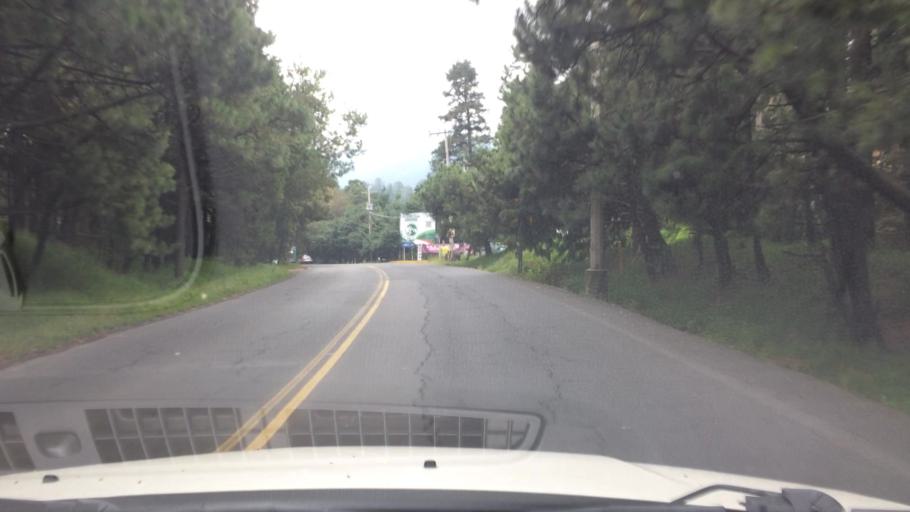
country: MX
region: Mexico City
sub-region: Tlalpan
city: Lomas de Tepemecatl
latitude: 19.2544
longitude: -99.2447
